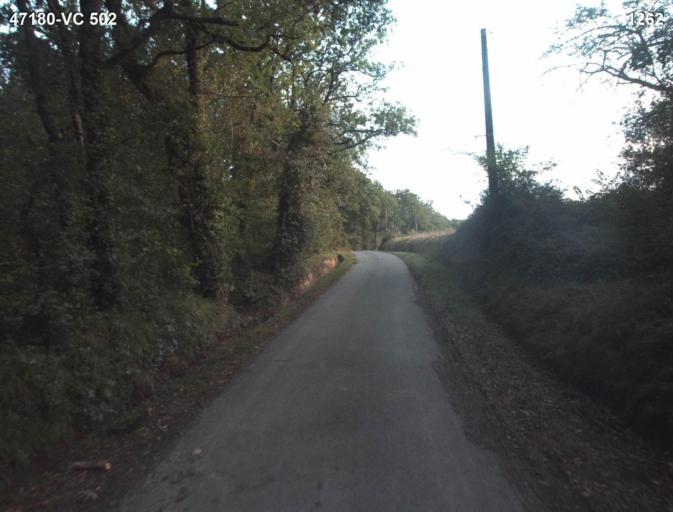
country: FR
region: Aquitaine
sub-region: Departement du Lot-et-Garonne
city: Sainte-Colombe-en-Bruilhois
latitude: 44.1691
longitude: 0.4795
